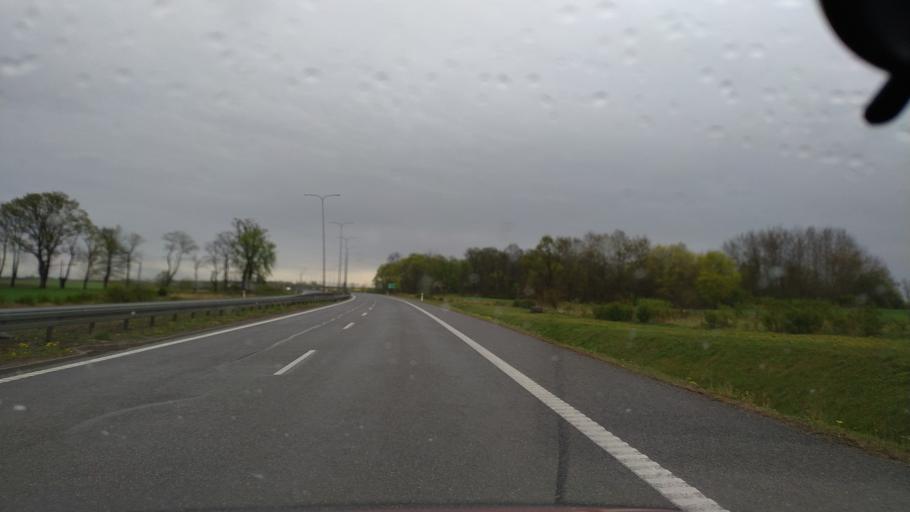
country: PL
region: Pomeranian Voivodeship
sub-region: Powiat chojnicki
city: Chojnice
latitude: 53.6791
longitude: 17.5784
